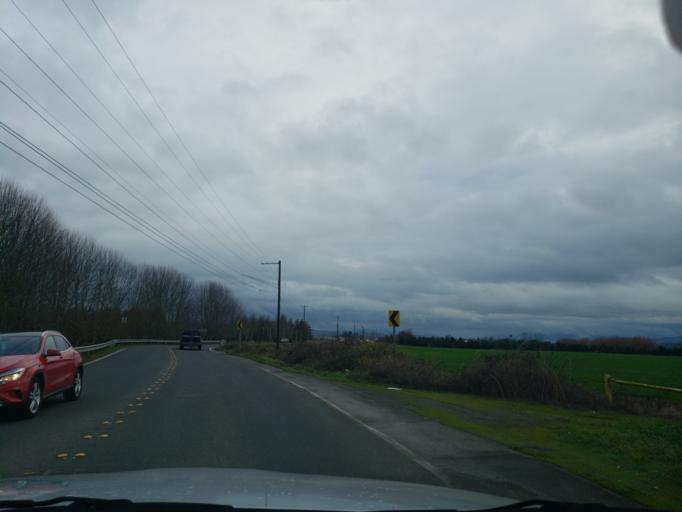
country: US
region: Washington
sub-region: Snohomish County
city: Snohomish
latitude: 47.8992
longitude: -122.1309
